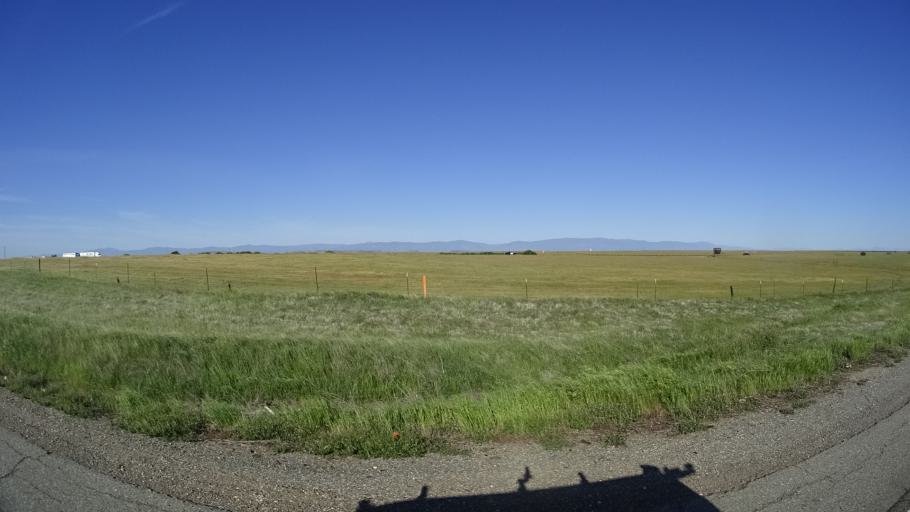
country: US
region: California
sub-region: Glenn County
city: Orland
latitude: 39.8085
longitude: -122.1973
